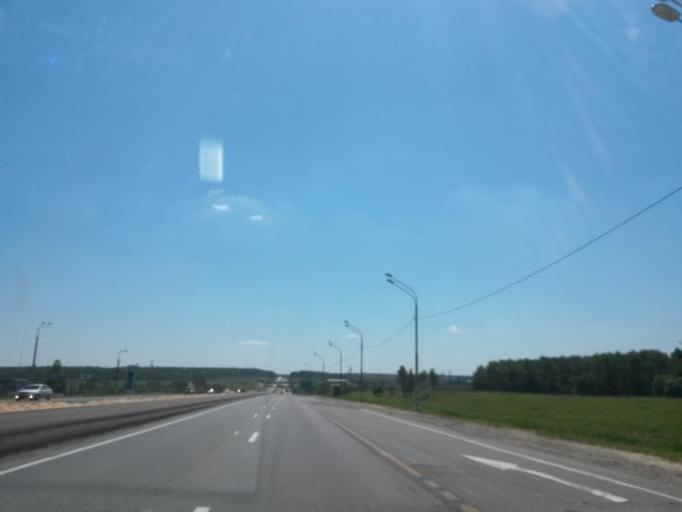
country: RU
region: Moskovskaya
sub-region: Chekhovskiy Rayon
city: Chekhov
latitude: 55.1403
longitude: 37.5587
